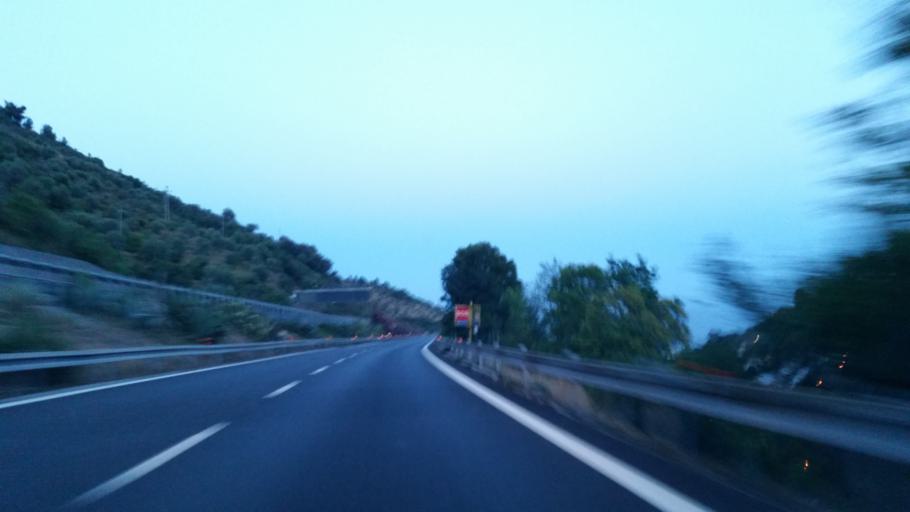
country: IT
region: Liguria
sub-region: Provincia di Imperia
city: San Remo
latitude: 43.8395
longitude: 7.7555
